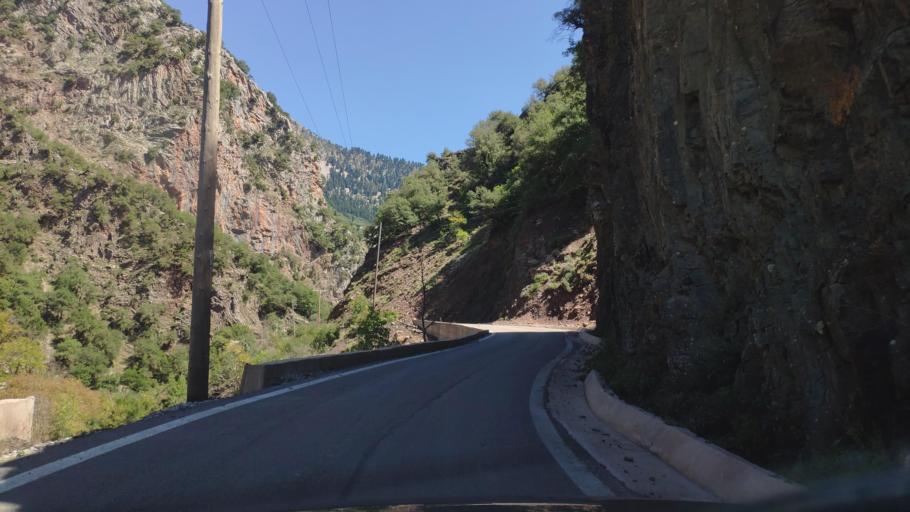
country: GR
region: Central Greece
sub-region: Nomos Evrytanias
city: Kerasochori
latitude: 39.1332
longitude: 21.6327
